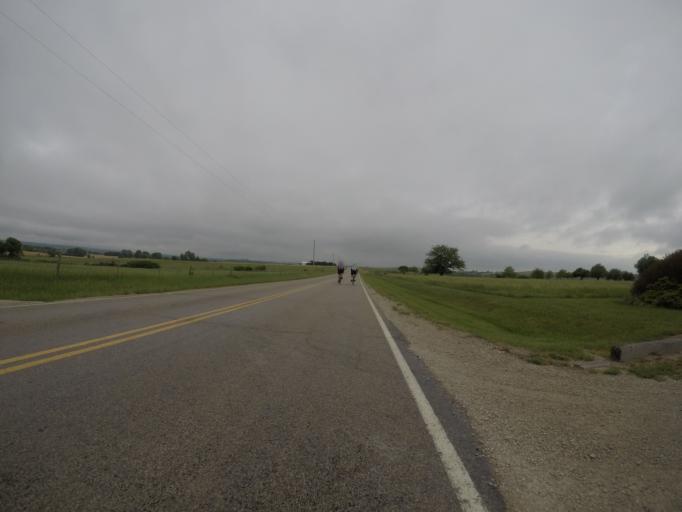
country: US
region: Kansas
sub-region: Pottawatomie County
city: Westmoreland
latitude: 39.4581
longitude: -96.1840
